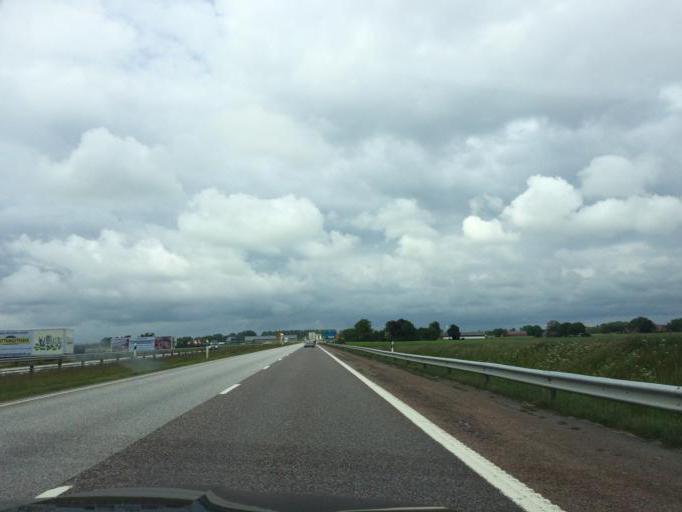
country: SE
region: Skane
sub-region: Angelholms Kommun
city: Strovelstorp
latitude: 56.1826
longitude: 12.8504
